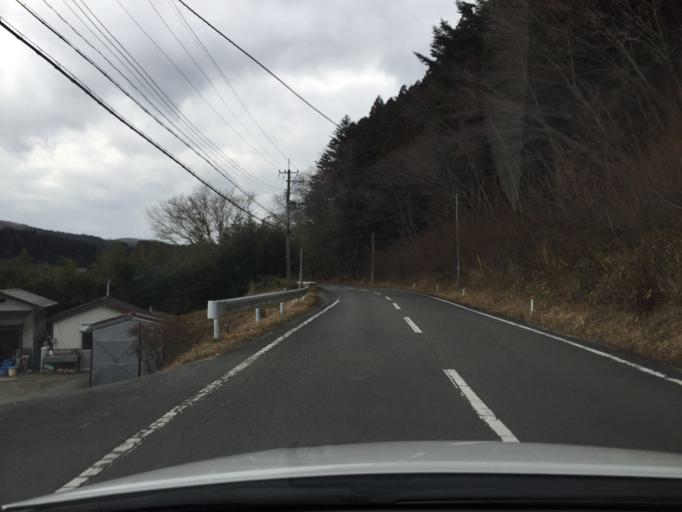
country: JP
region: Fukushima
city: Iwaki
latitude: 37.1770
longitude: 140.7248
